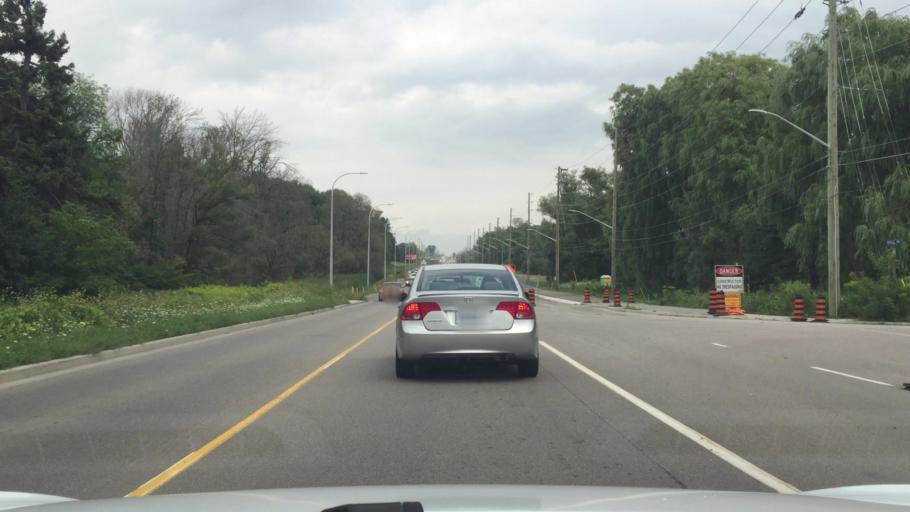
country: CA
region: Ontario
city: Ajax
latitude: 43.8537
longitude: -78.9742
